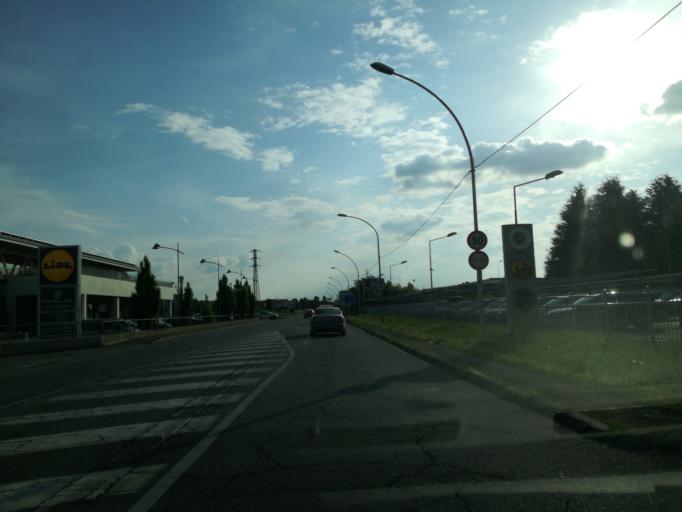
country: IT
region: Lombardy
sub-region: Provincia di Bergamo
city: Calusco d'Adda
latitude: 45.6867
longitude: 9.4636
